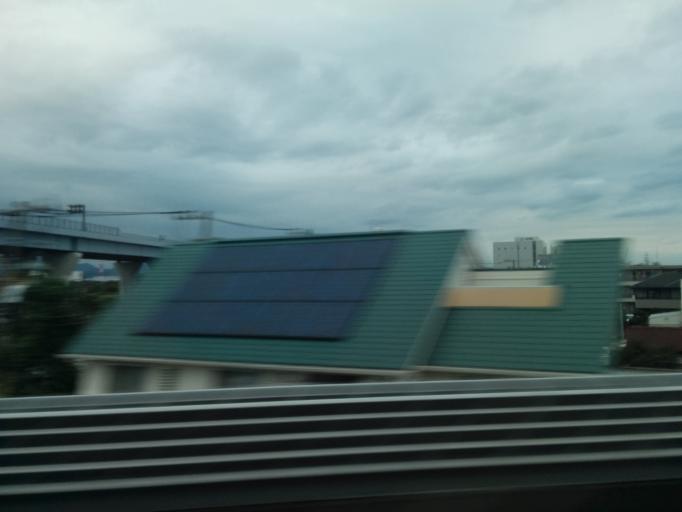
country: JP
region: Kanagawa
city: Atsugi
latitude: 35.3933
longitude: 139.3783
